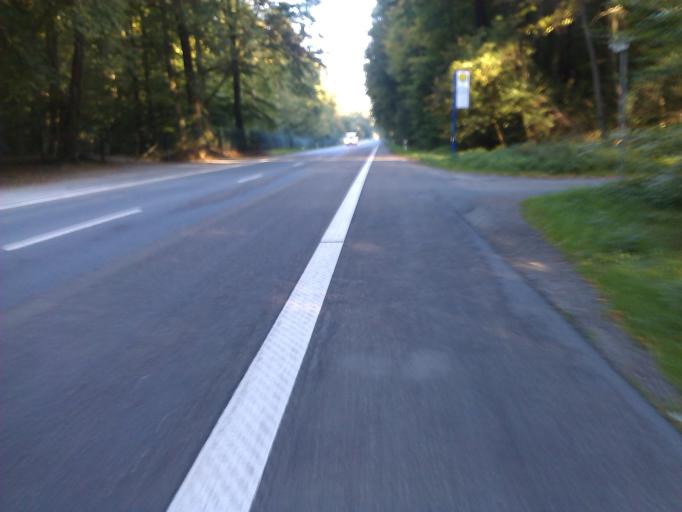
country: DE
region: Hesse
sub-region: Regierungsbezirk Darmstadt
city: Erzhausen
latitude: 49.9802
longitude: 8.6437
